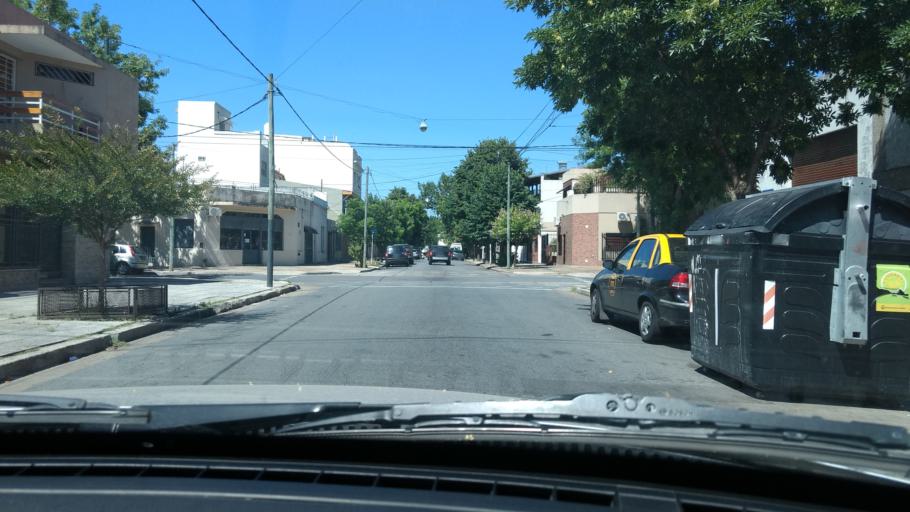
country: AR
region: Buenos Aires F.D.
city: Villa Santa Rita
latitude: -34.6257
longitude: -58.5172
